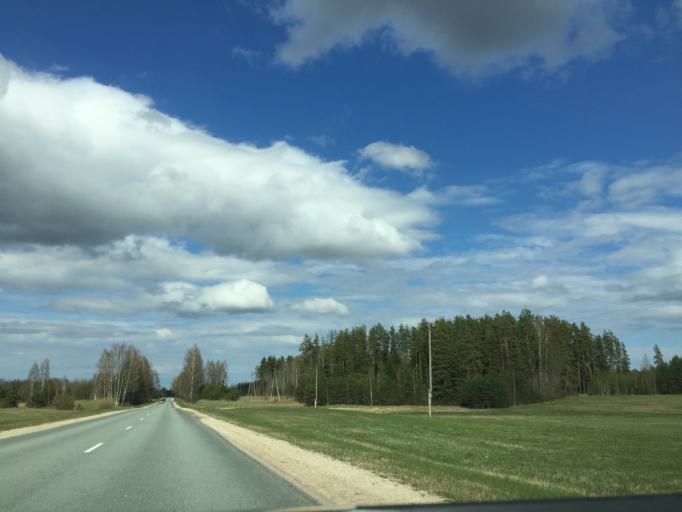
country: LV
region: Gulbenes Rajons
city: Gulbene
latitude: 57.2642
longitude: 26.5614
